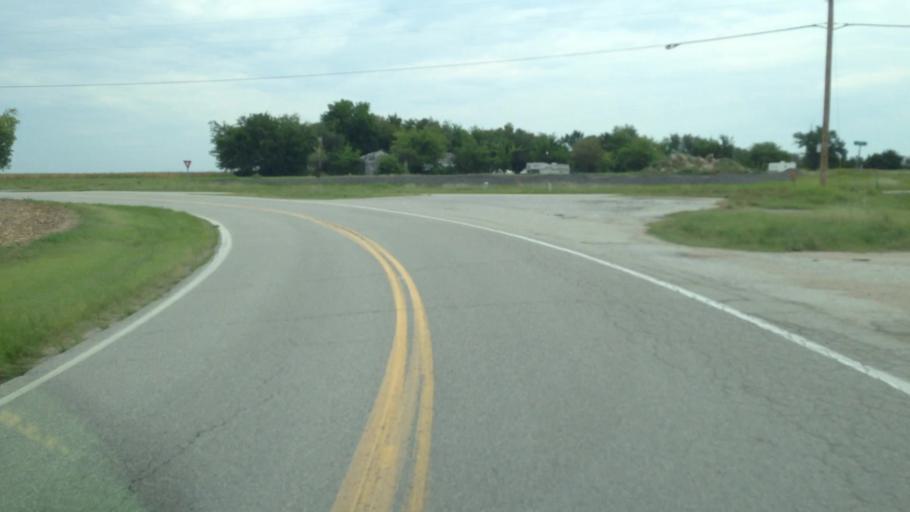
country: US
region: Oklahoma
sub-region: Delaware County
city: Cleora
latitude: 36.6266
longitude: -94.9816
